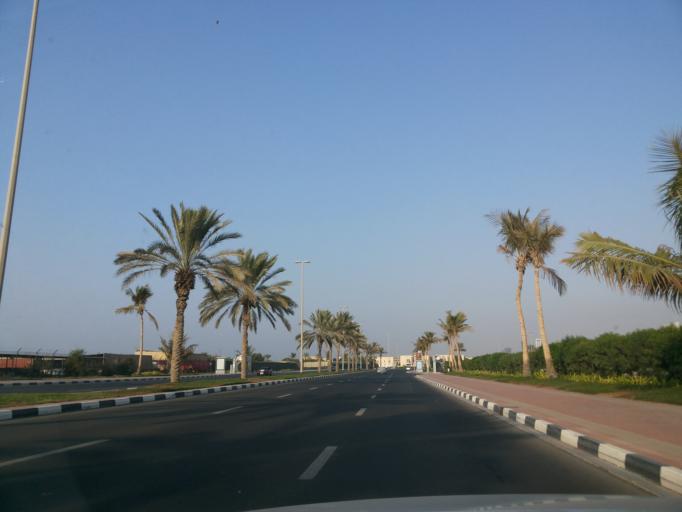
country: AE
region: Ash Shariqah
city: Sharjah
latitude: 25.3047
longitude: 55.3395
